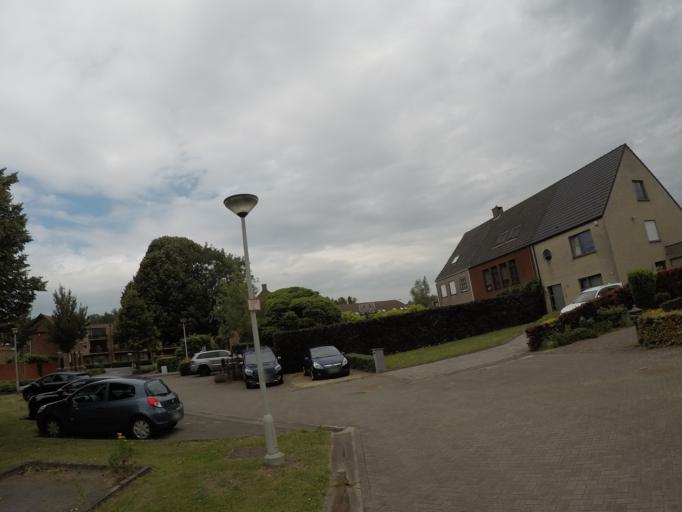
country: BE
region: Flanders
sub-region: Provincie Antwerpen
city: Kapellen
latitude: 51.3037
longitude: 4.4133
